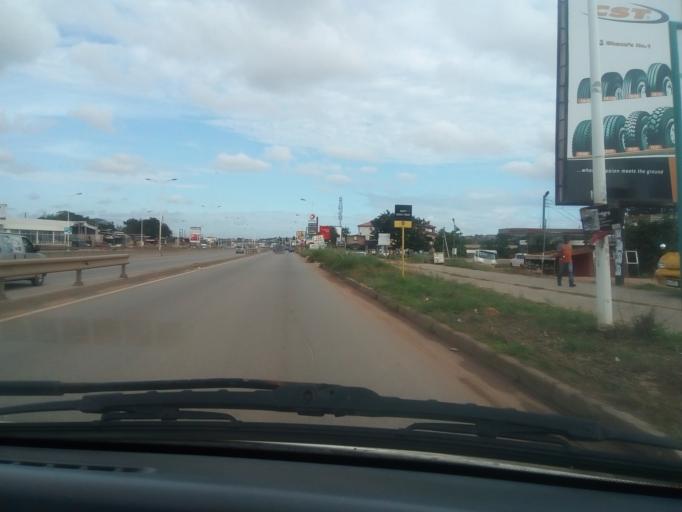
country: GH
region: Greater Accra
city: Dome
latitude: 5.6562
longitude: -0.2635
